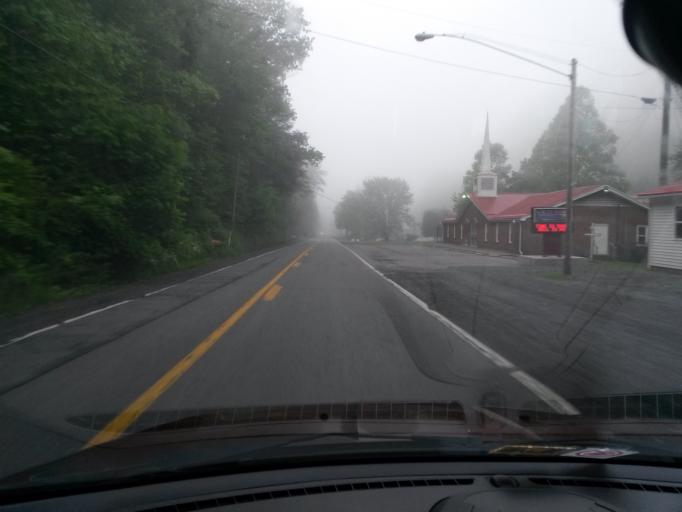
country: US
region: West Virginia
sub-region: McDowell County
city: Welch
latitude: 37.4710
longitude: -81.5417
